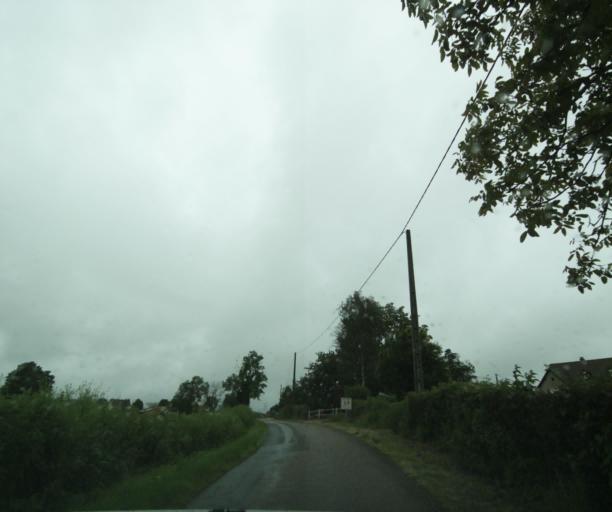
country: FR
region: Bourgogne
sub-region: Departement de Saone-et-Loire
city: Charolles
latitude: 46.4230
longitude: 4.2996
